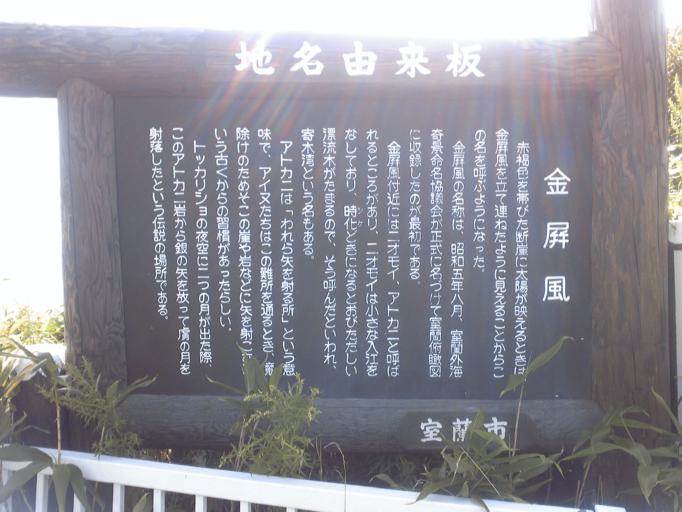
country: JP
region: Hokkaido
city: Muroran
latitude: 42.3047
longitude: 141.0035
